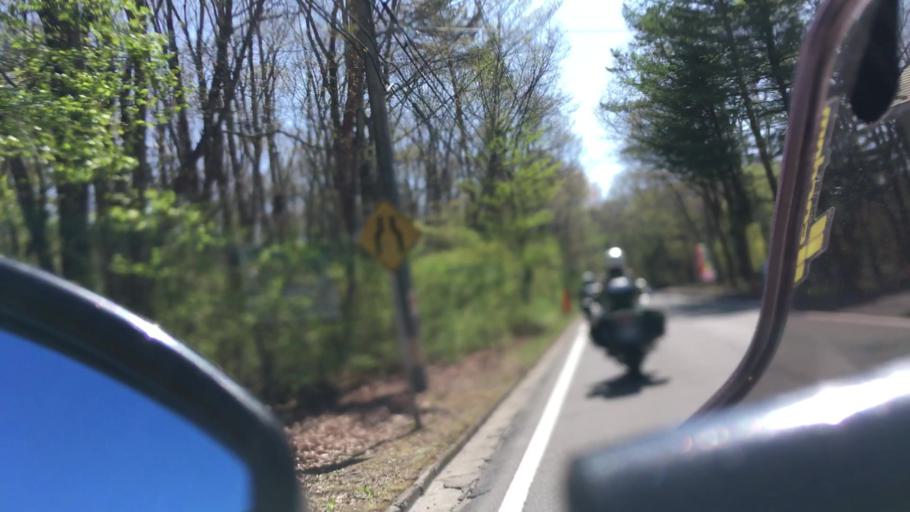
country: JP
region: Nagano
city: Komoro
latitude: 36.4658
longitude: 138.5594
